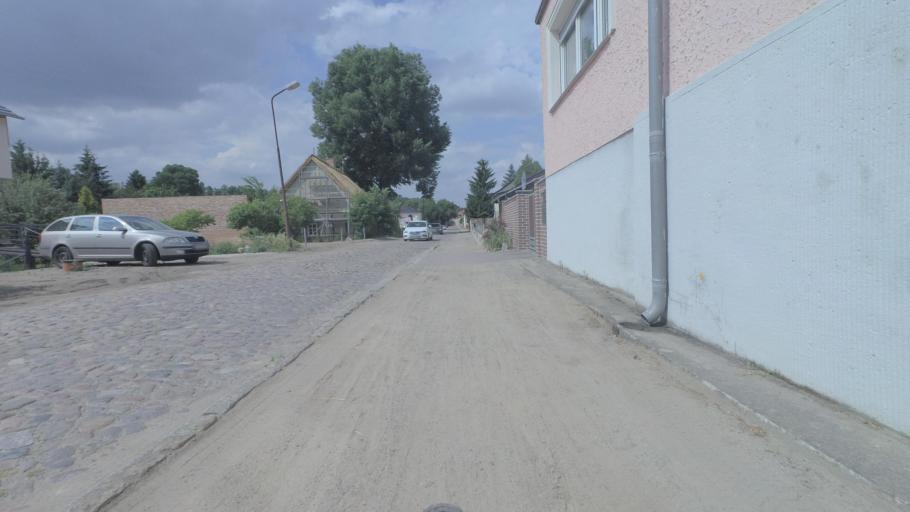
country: DE
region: Brandenburg
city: Zossen
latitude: 52.2094
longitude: 13.4665
